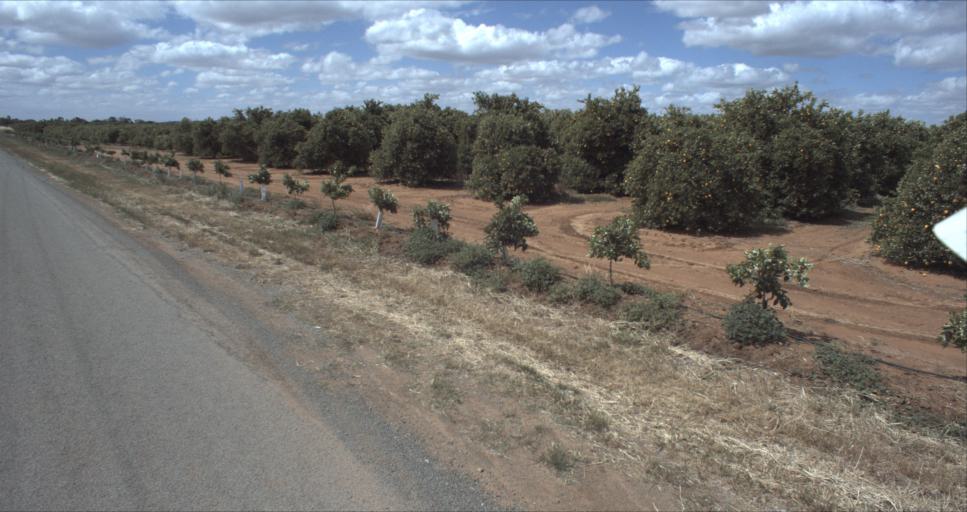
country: AU
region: New South Wales
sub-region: Leeton
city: Leeton
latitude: -34.5841
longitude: 146.3917
